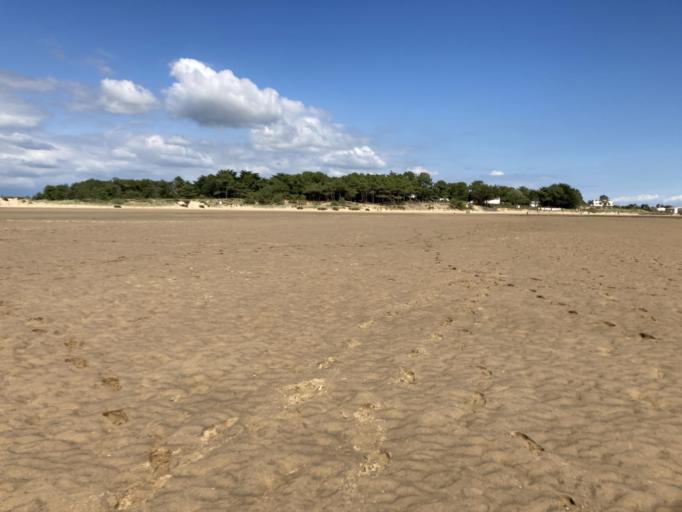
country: FR
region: Pays de la Loire
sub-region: Departement de la Vendee
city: Saint-Hilaire-de-Talmont
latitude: 46.4336
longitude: -1.6428
